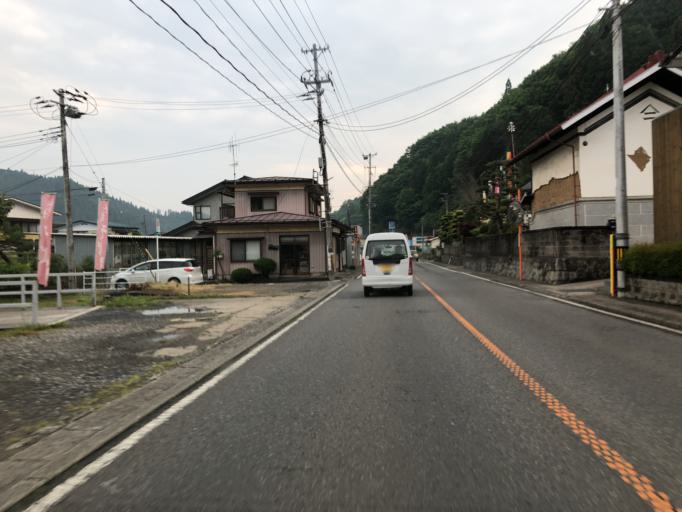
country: JP
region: Fukushima
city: Ishikawa
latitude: 37.1496
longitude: 140.4668
